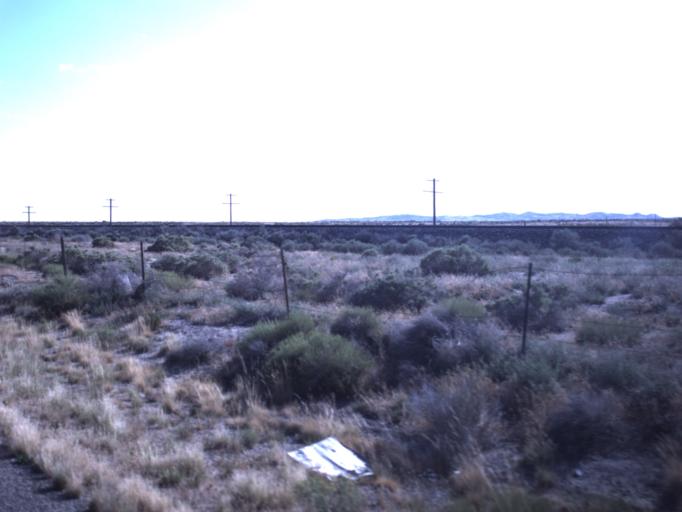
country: US
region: Utah
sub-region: Beaver County
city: Milford
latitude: 38.6782
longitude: -112.9787
